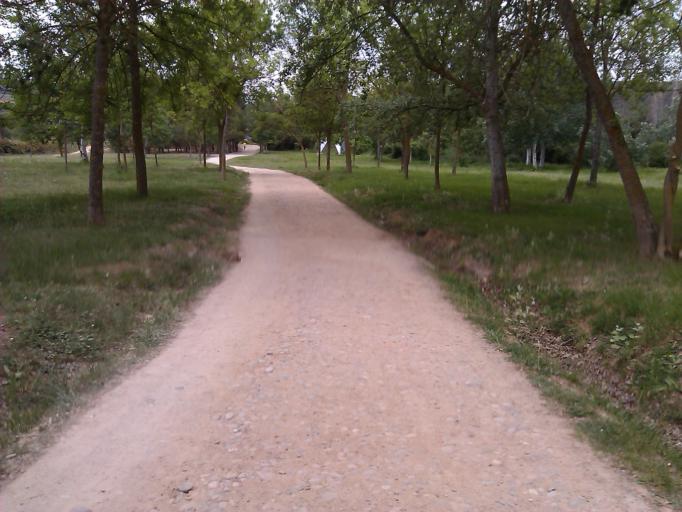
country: ES
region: La Rioja
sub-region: Provincia de La Rioja
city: Lardero
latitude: 42.4471
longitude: -2.5086
